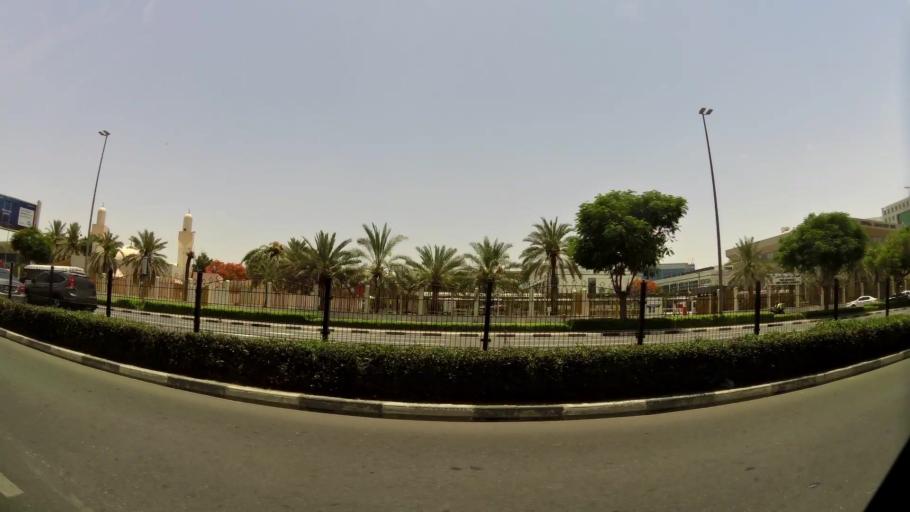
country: AE
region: Ash Shariqah
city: Sharjah
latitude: 25.2435
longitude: 55.3072
